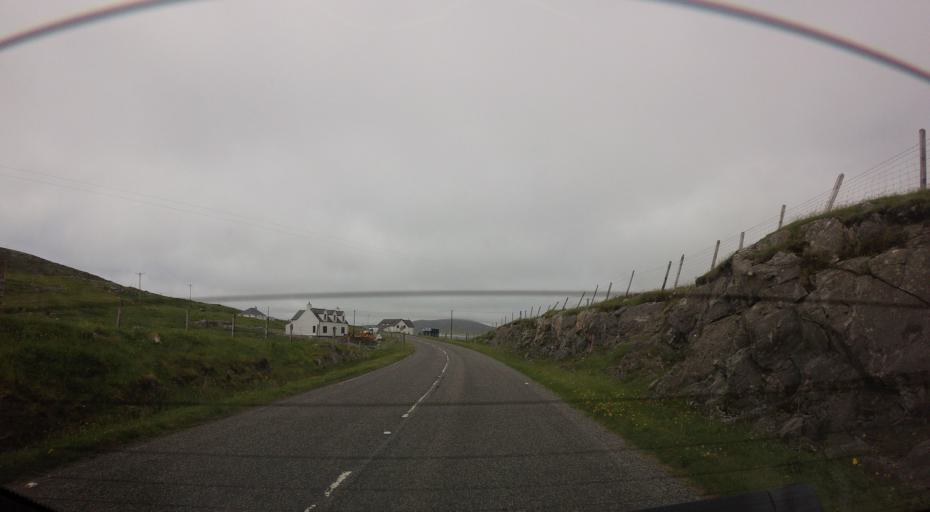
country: GB
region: Scotland
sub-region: Eilean Siar
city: Harris
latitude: 57.8660
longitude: -6.9542
